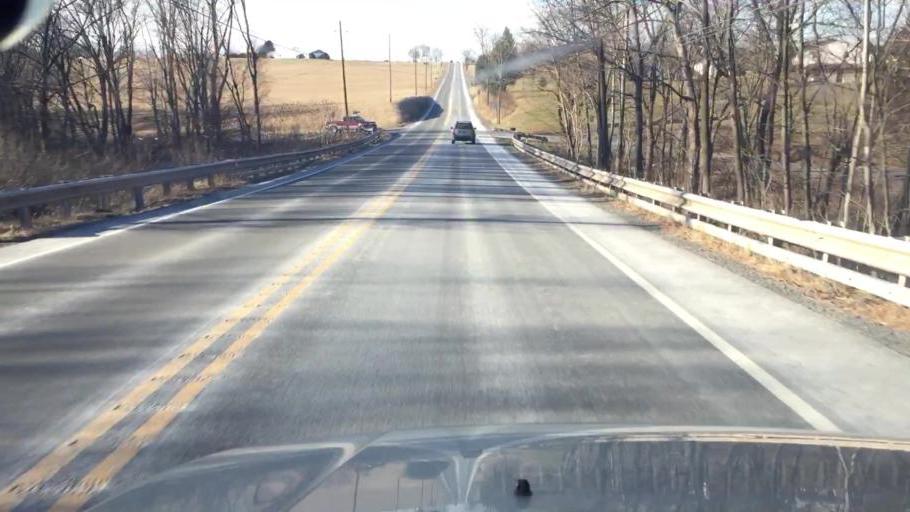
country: US
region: Pennsylvania
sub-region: Luzerne County
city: Nescopeck
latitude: 41.0363
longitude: -76.1349
